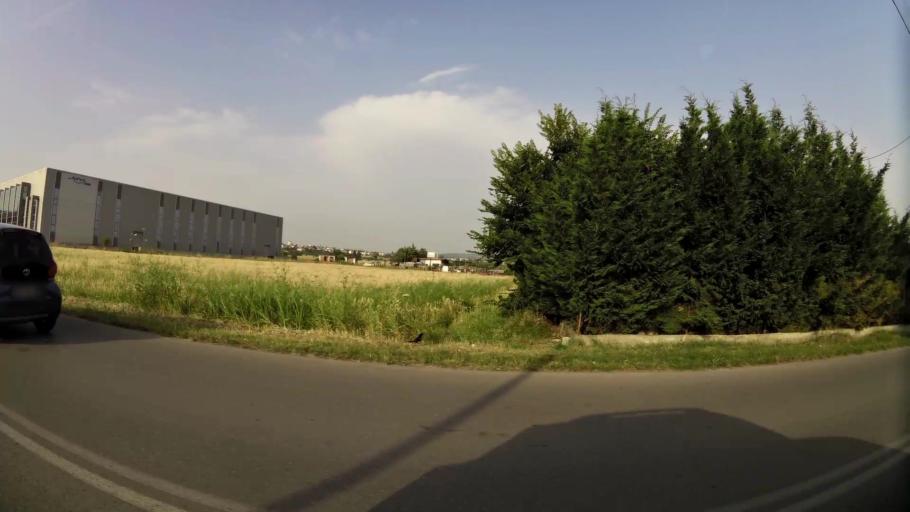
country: GR
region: Central Macedonia
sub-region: Nomos Thessalonikis
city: Oraiokastro
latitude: 40.7054
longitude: 22.9128
